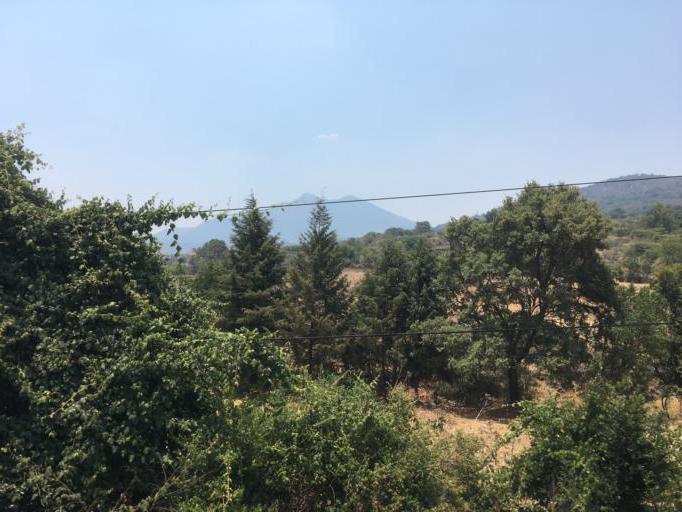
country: MX
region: Michoacan
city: Quiroga
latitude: 19.6605
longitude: -101.5110
